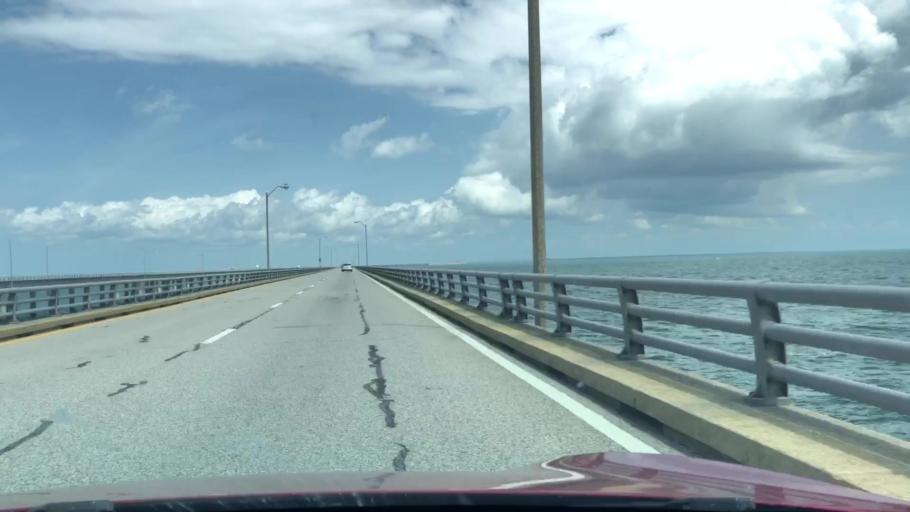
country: US
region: Virginia
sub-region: City of Virginia Beach
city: Virginia Beach
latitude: 36.9991
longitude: -76.0990
